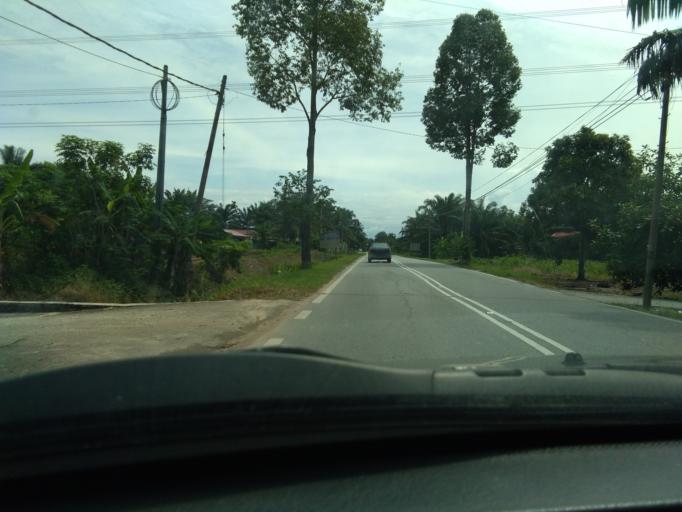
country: MY
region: Perak
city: Bagan Serai
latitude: 5.0533
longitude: 100.5903
